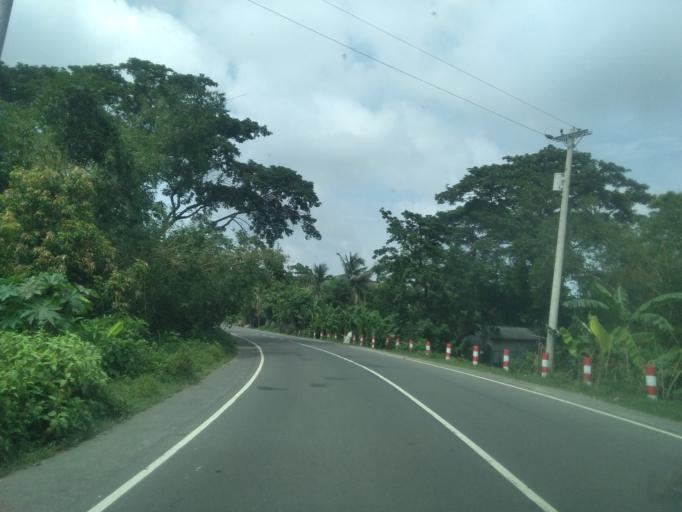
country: BD
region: Khulna
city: Kesabpur
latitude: 22.8193
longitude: 89.2619
